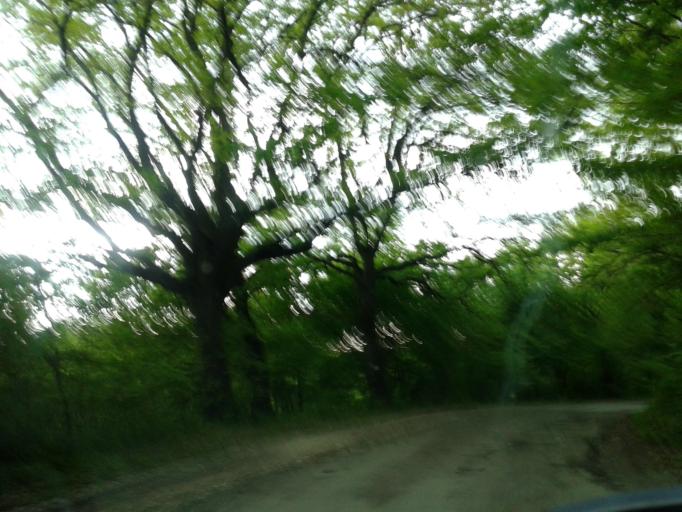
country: HU
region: Komarom-Esztergom
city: Kesztolc
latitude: 47.7069
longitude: 18.8261
